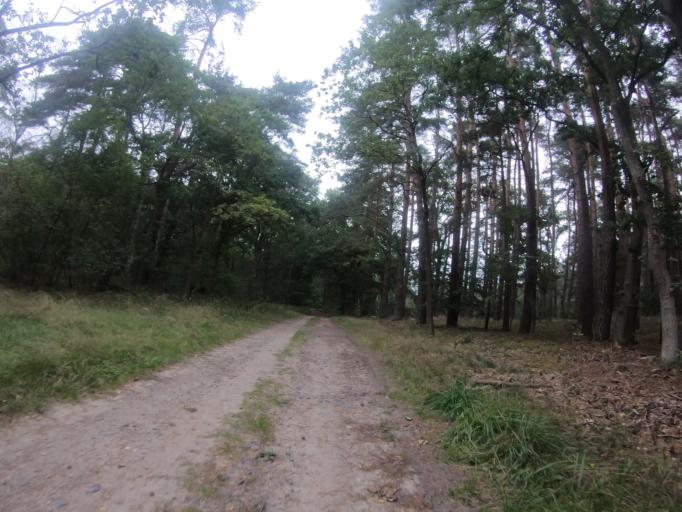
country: DE
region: Lower Saxony
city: Ribbesbuttel
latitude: 52.4526
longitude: 10.5243
